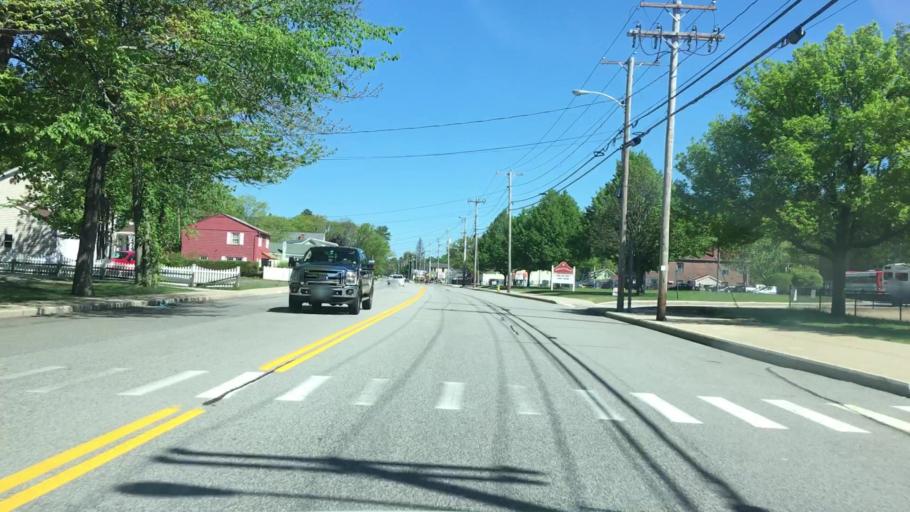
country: US
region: Maine
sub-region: York County
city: Springvale
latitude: 43.4519
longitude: -70.7882
